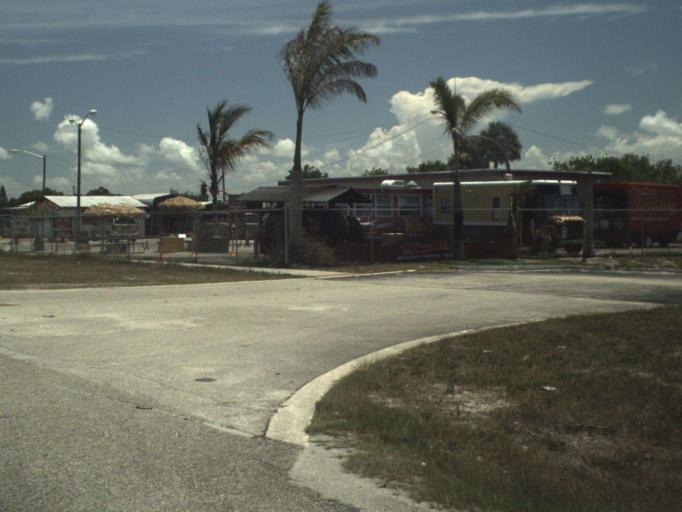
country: US
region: Florida
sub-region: Saint Lucie County
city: Fort Pierce North
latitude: 27.4842
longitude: -80.3409
